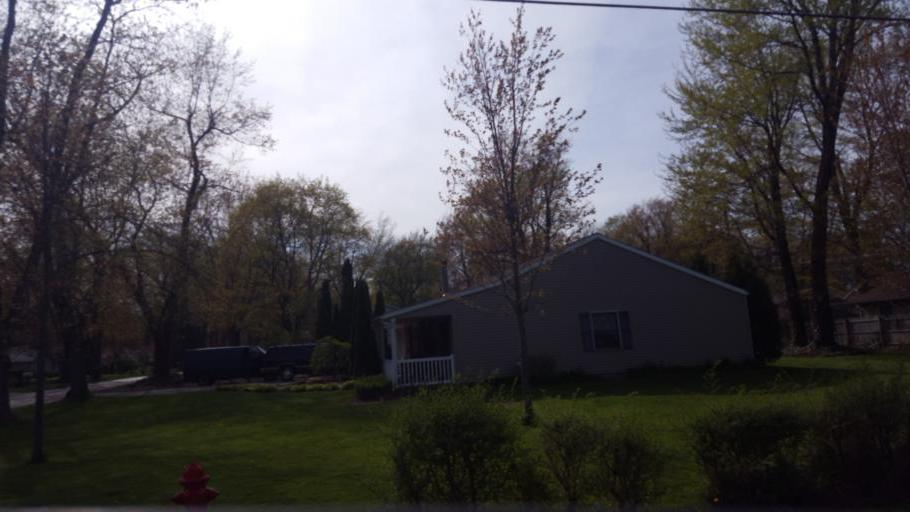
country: US
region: Ohio
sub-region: Lake County
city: North Madison
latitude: 41.8296
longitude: -81.0618
